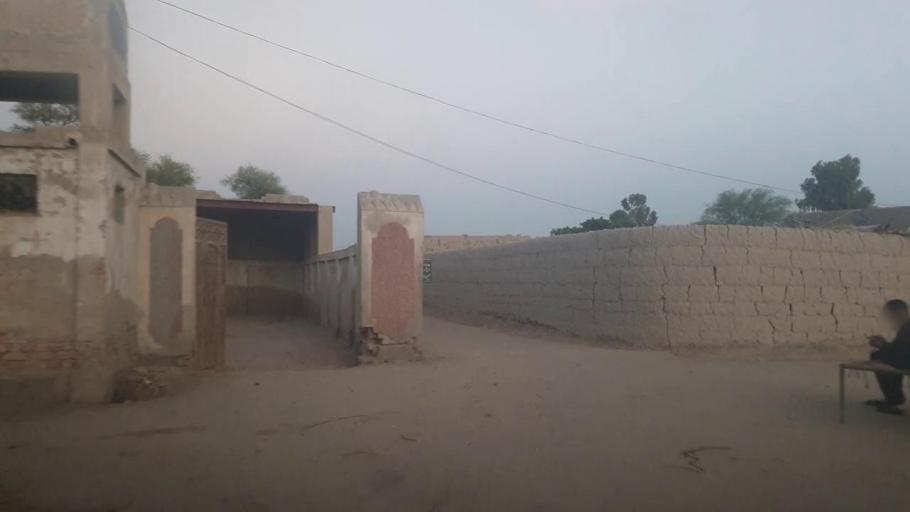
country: PK
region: Sindh
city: Ubauro
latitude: 28.1034
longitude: 69.7826
